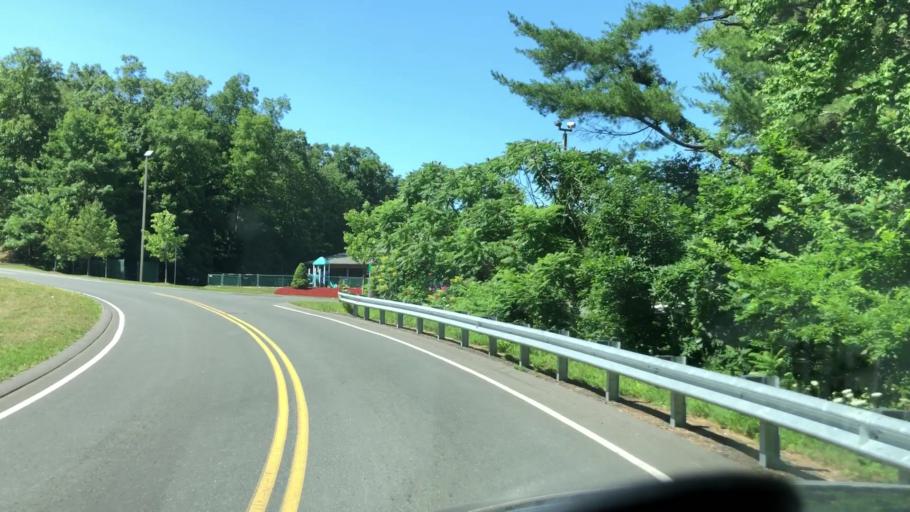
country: US
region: Massachusetts
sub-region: Hampden County
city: Holyoke
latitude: 42.1902
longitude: -72.6528
